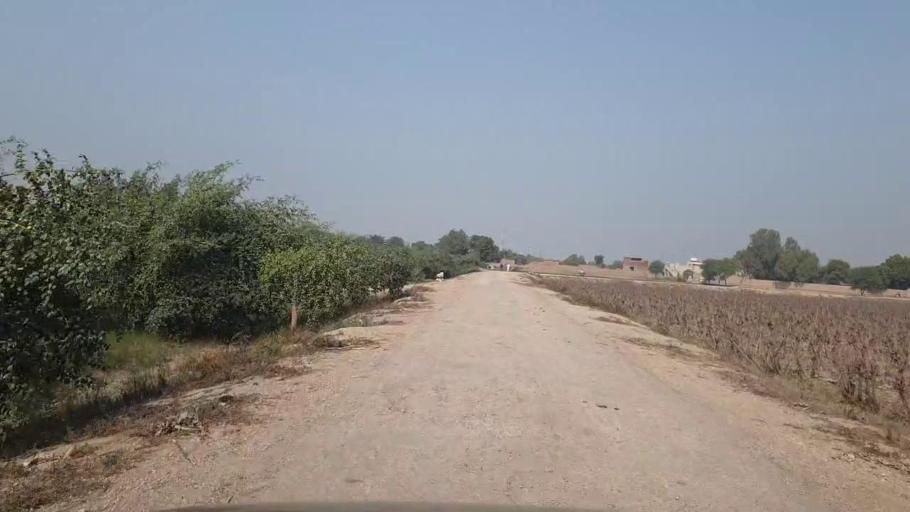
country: PK
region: Sindh
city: Bhit Shah
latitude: 25.7969
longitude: 68.4966
